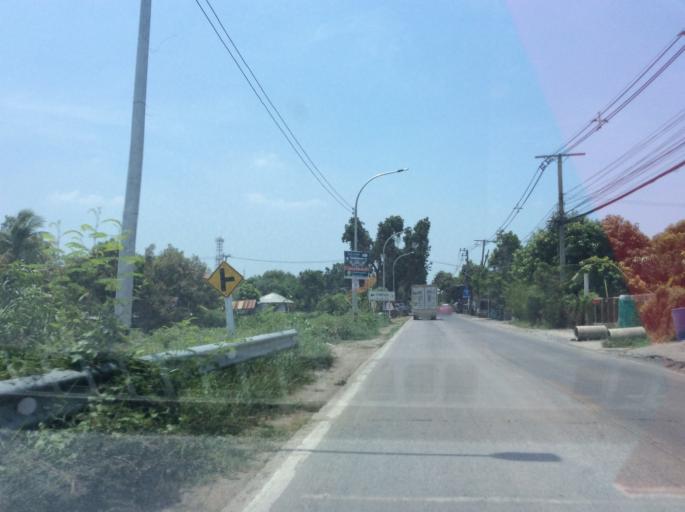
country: TH
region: Pathum Thani
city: Ban Rangsit
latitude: 14.0340
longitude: 100.7789
